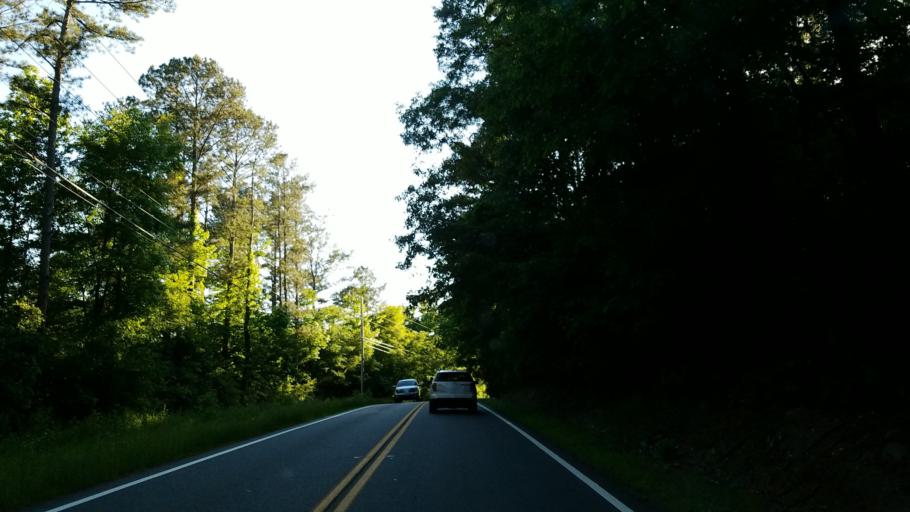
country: US
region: Georgia
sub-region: Cherokee County
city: Holly Springs
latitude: 34.1644
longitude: -84.5772
